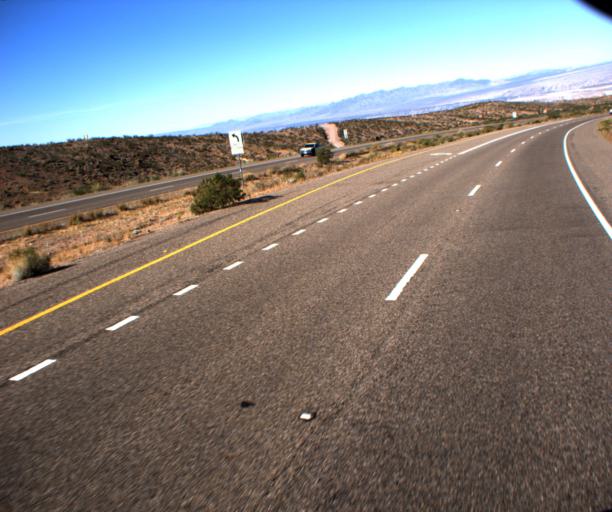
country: US
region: Nevada
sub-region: Clark County
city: Laughlin
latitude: 35.1862
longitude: -114.4533
